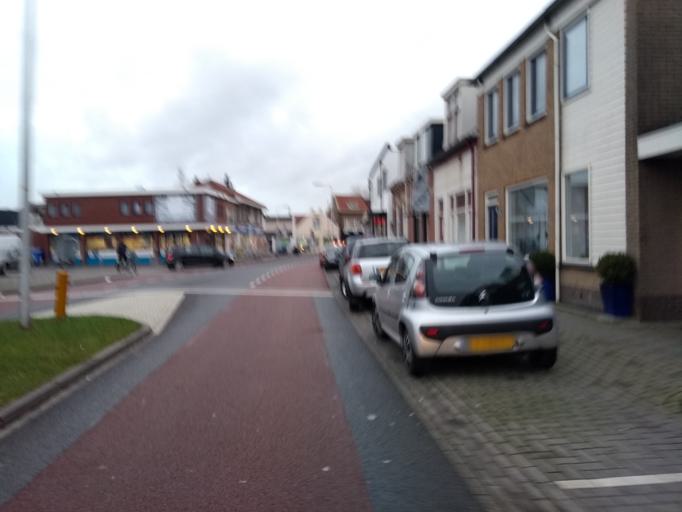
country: NL
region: Overijssel
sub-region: Gemeente Almelo
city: Almelo
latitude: 52.3495
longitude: 6.6614
